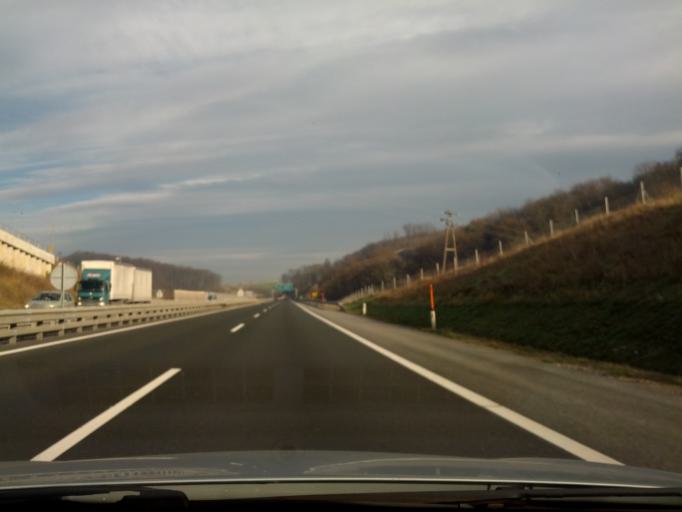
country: SI
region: Pesnica
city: Pesnica pri Mariboru
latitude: 46.5706
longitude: 15.6871
